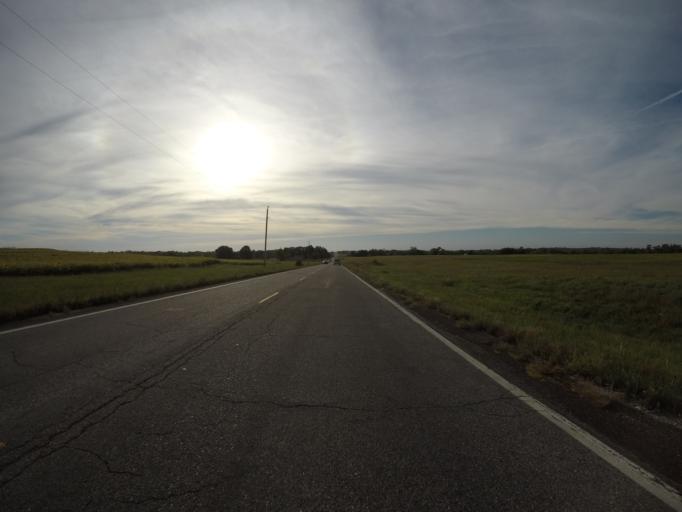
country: US
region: Kansas
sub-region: Douglas County
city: Baldwin City
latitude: 38.7823
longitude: -95.2088
